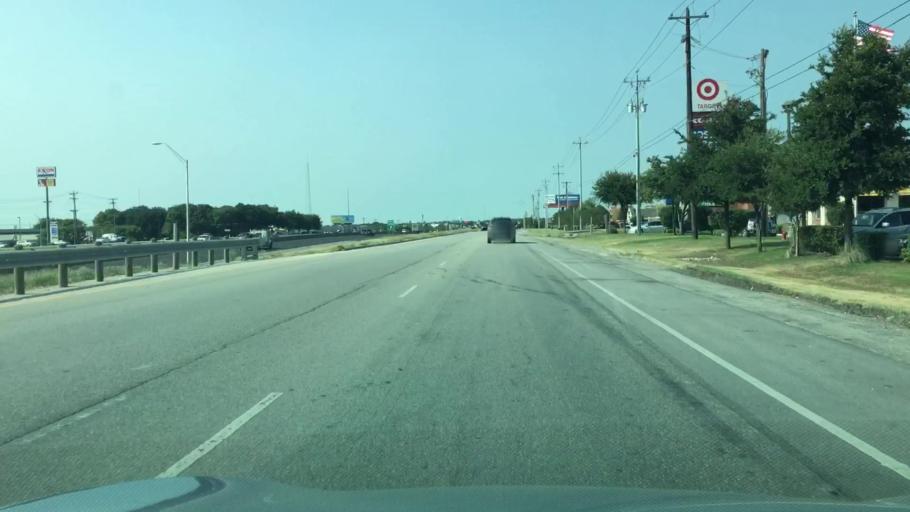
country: US
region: Texas
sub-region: Hays County
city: Kyle
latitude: 30.0118
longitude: -97.8620
